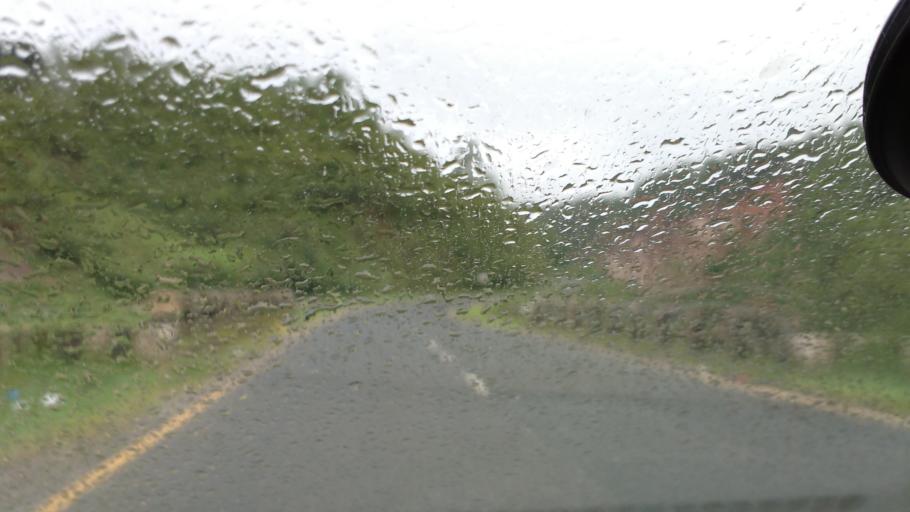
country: IN
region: Meghalaya
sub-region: East Khasi Hills
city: Shillong
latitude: 25.4528
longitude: 91.8211
